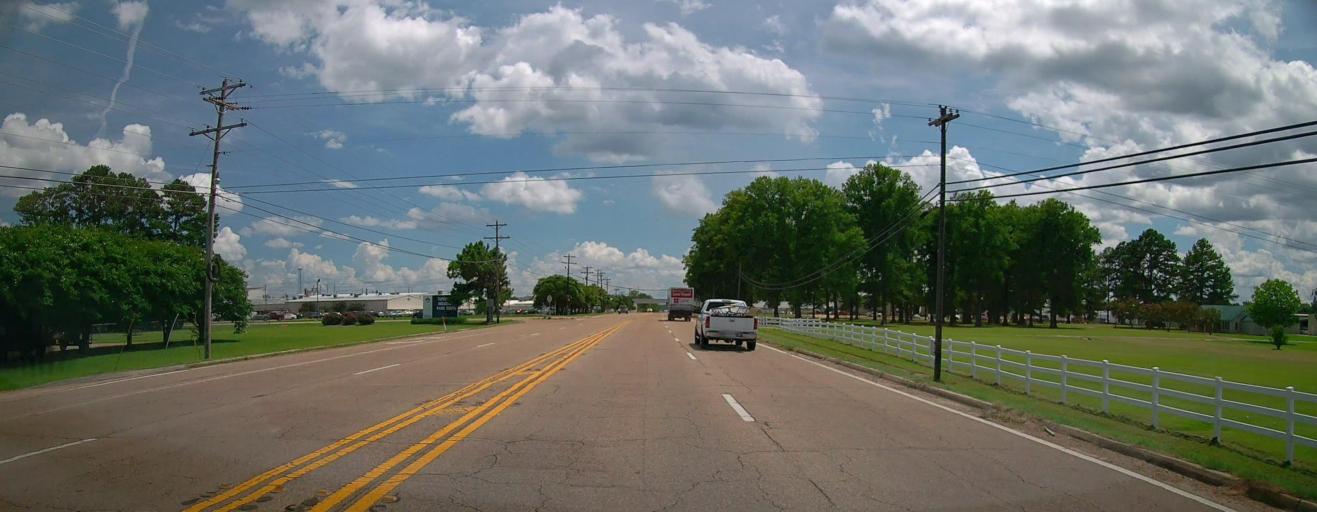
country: US
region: Mississippi
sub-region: Lee County
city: Verona
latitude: 34.1649
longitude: -88.7195
